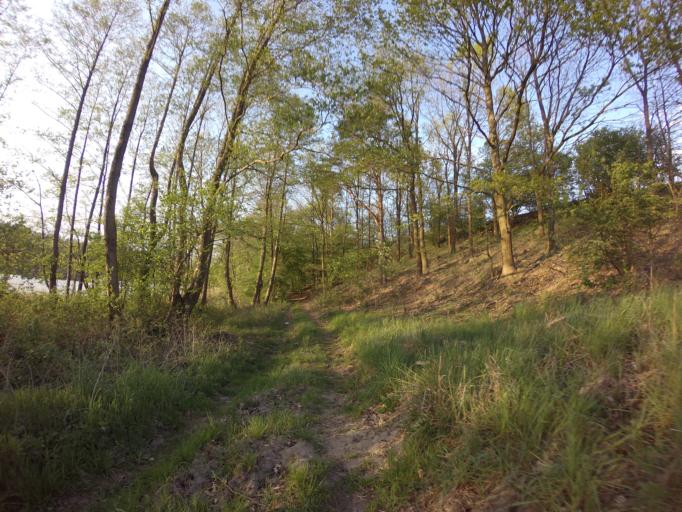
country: PL
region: West Pomeranian Voivodeship
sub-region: Powiat choszczenski
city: Choszczno
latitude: 53.1478
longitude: 15.3468
